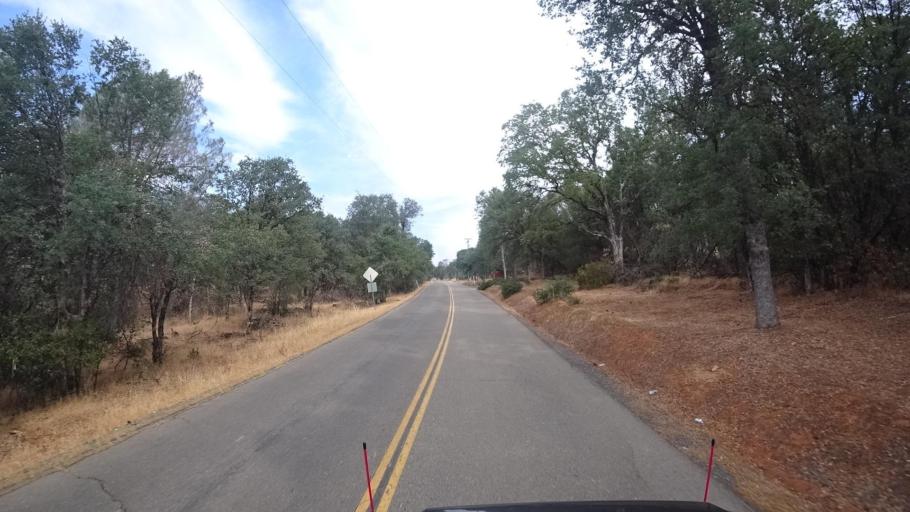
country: US
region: California
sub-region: Mariposa County
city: Midpines
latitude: 37.5335
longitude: -119.9548
